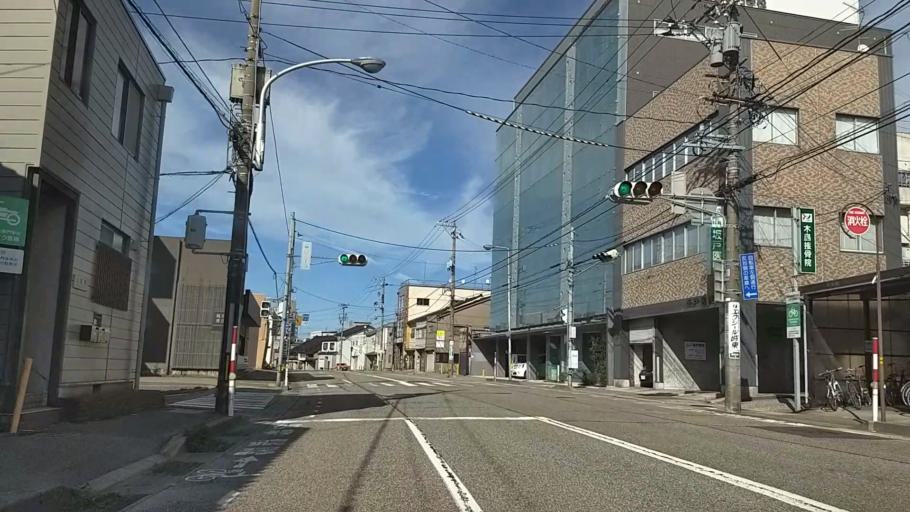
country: JP
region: Ishikawa
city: Kanazawa-shi
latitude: 36.5779
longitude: 136.6693
